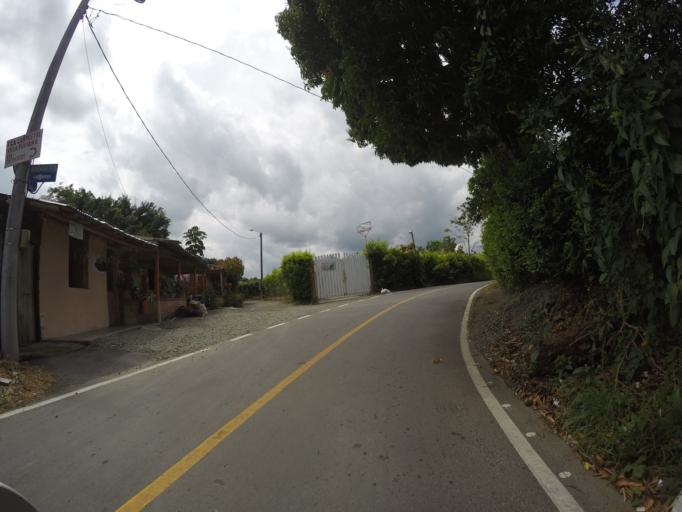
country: CO
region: Quindio
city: Quimbaya
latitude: 4.6130
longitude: -75.7521
